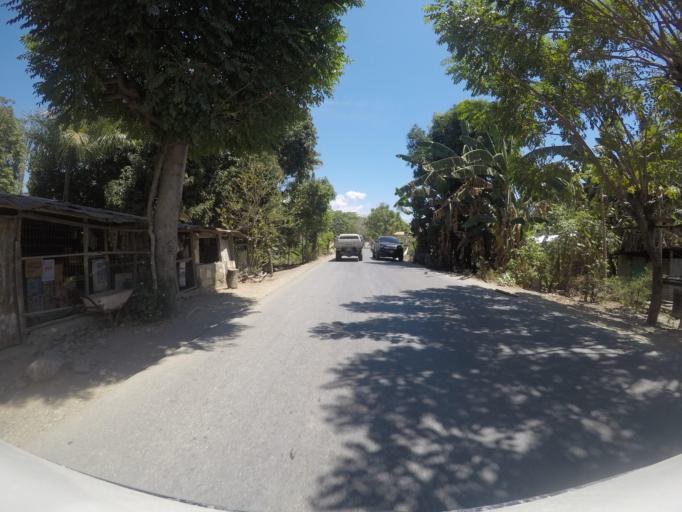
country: ID
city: Metinaro
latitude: -8.5466
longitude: 125.6686
